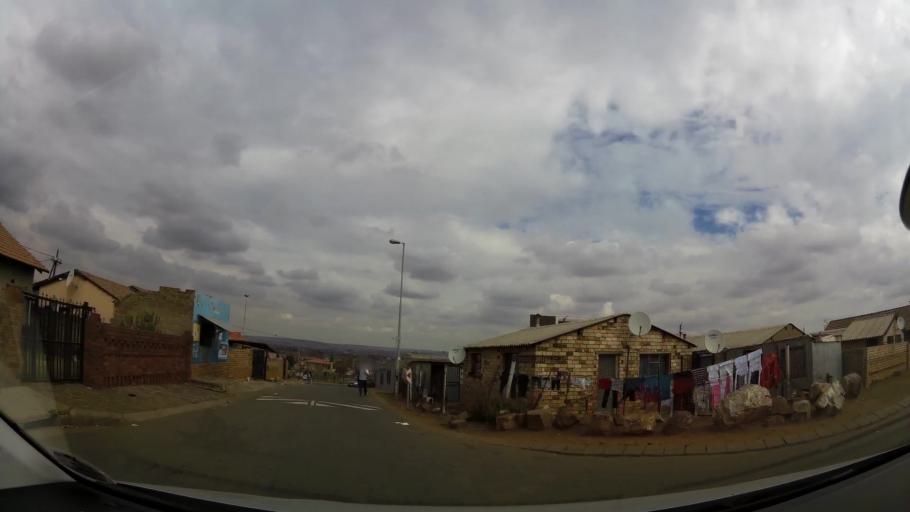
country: ZA
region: Gauteng
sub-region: City of Johannesburg Metropolitan Municipality
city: Soweto
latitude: -26.2800
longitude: 27.8586
